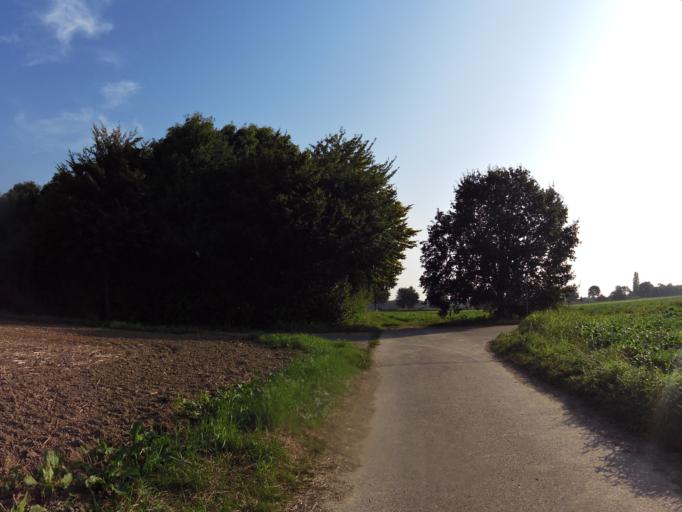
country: DE
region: North Rhine-Westphalia
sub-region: Regierungsbezirk Koln
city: Ubach-Palenberg
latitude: 50.9473
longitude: 6.0900
